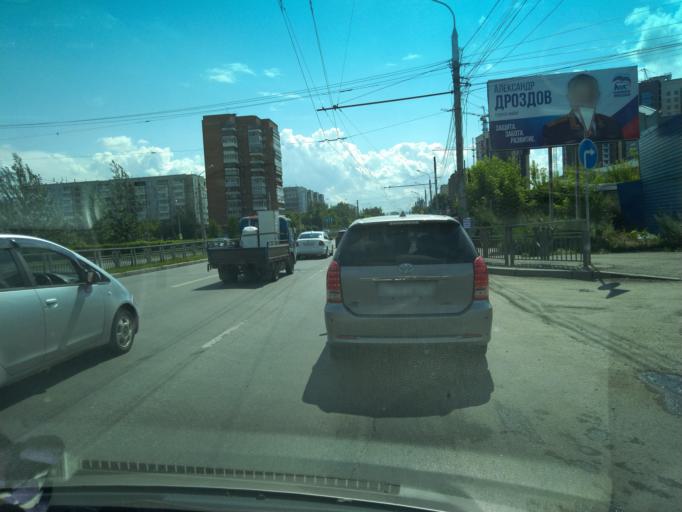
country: RU
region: Krasnoyarskiy
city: Solnechnyy
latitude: 56.0557
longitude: 92.9412
